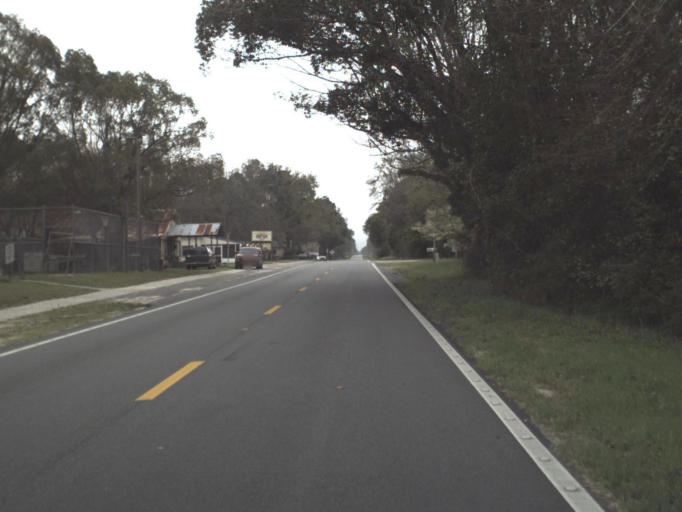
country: US
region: Florida
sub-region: Gulf County
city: Wewahitchka
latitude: 30.0212
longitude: -84.9798
